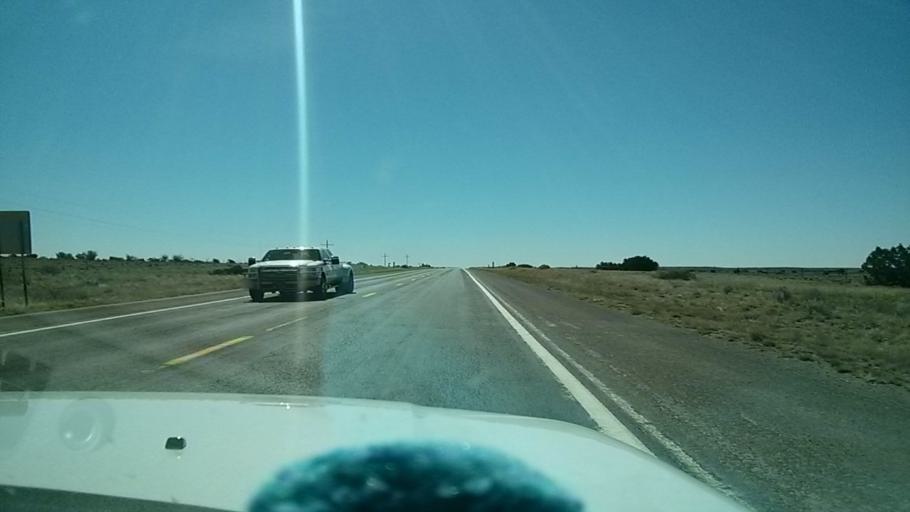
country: US
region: Arizona
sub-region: Mohave County
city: Peach Springs
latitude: 35.5415
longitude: -113.2731
